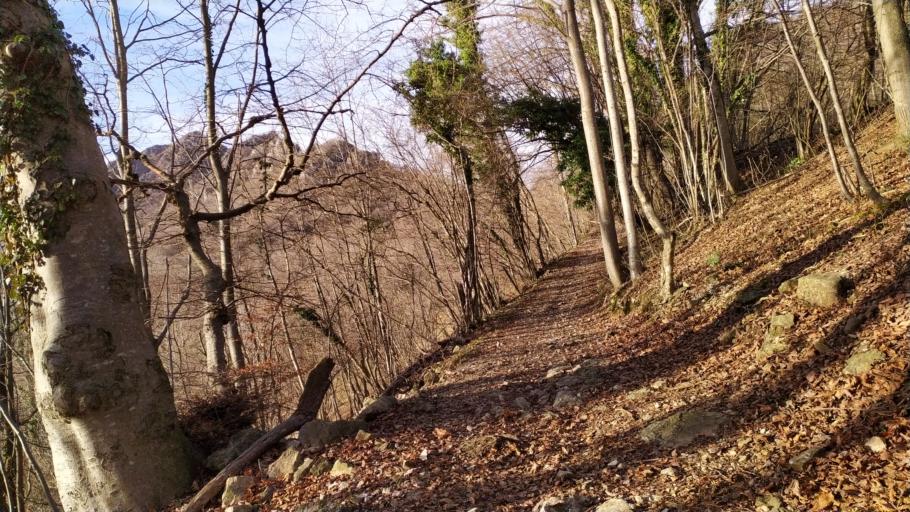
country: IT
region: Veneto
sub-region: Provincia di Vicenza
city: Velo d'Astico
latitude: 45.7663
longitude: 11.3560
